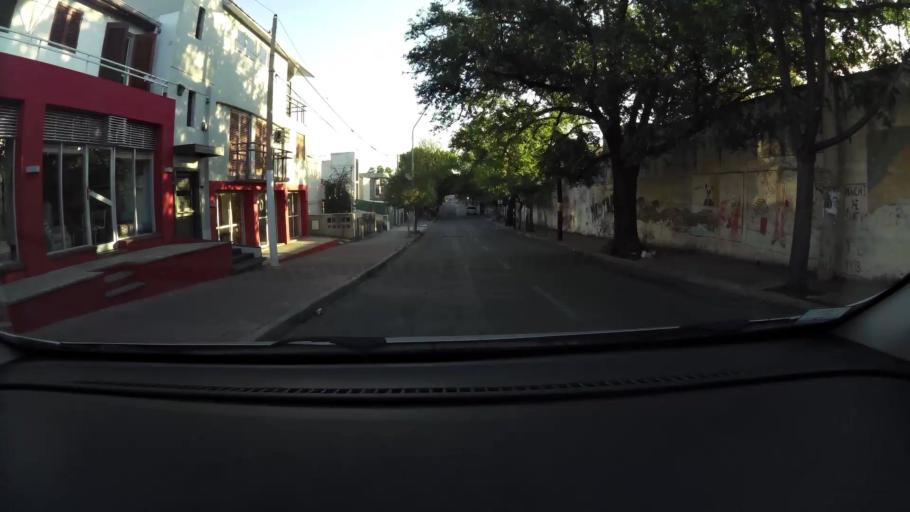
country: AR
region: Cordoba
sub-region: Departamento de Capital
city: Cordoba
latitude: -31.3831
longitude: -64.2164
